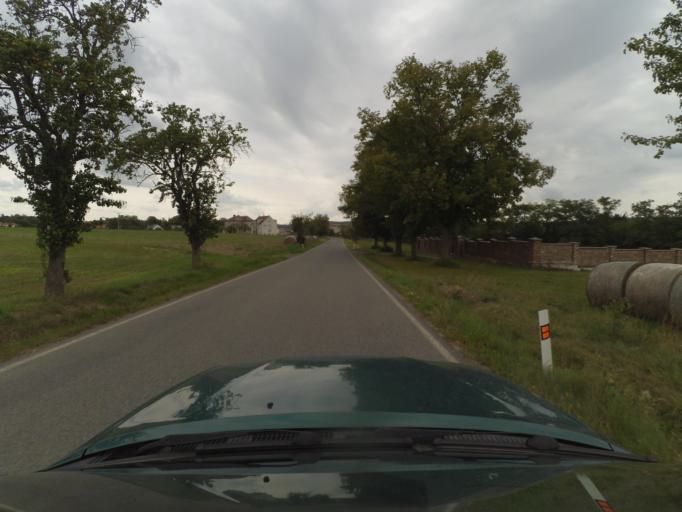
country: CZ
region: Plzensky
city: Hromnice
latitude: 49.8803
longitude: 13.5093
